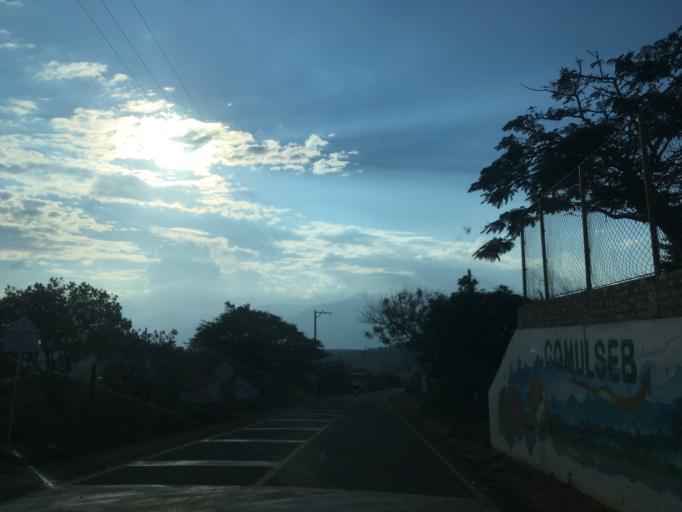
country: CO
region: Santander
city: Barichara
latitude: 6.6411
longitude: -73.1916
